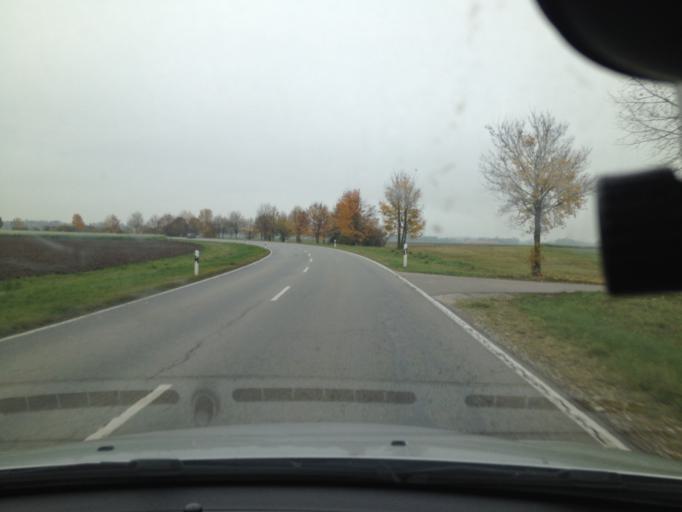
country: DE
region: Bavaria
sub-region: Swabia
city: Schwabmunchen
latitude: 48.1666
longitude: 10.7397
